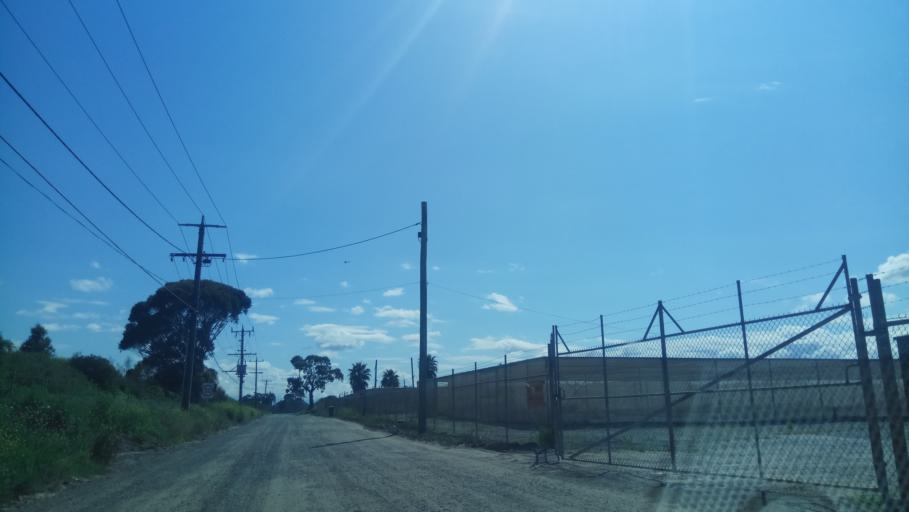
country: AU
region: Victoria
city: Heatherton
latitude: -37.9648
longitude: 145.1167
